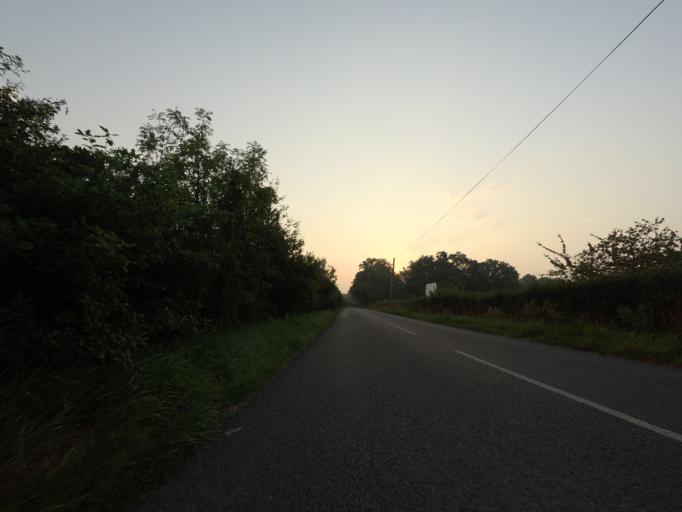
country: GB
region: England
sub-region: Kent
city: Headcorn
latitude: 51.1728
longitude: 0.6327
